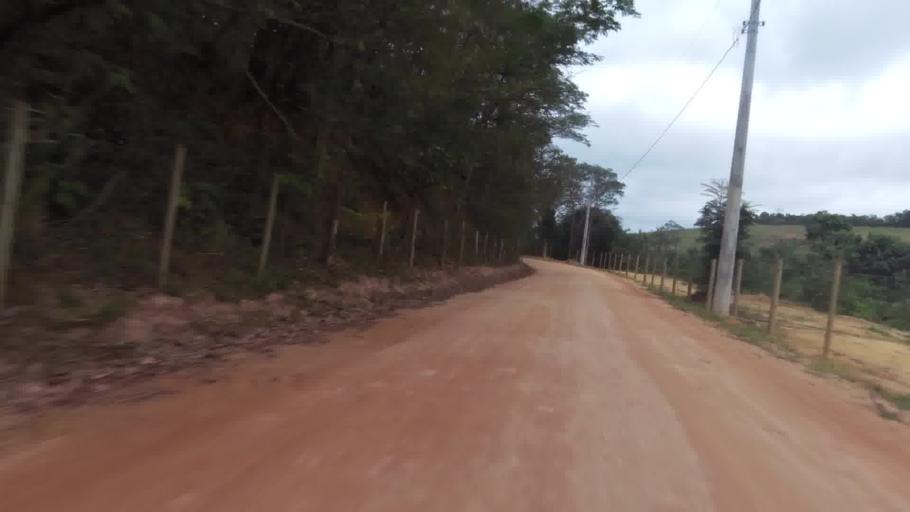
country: BR
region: Espirito Santo
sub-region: Alfredo Chaves
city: Alfredo Chaves
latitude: -20.6898
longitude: -40.7101
